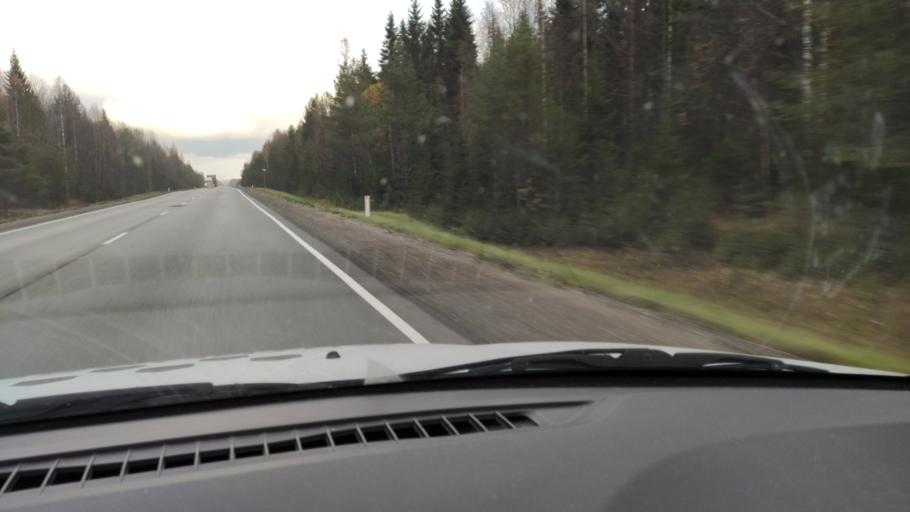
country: RU
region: Kirov
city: Chernaya Kholunitsa
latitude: 58.8151
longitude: 51.8241
